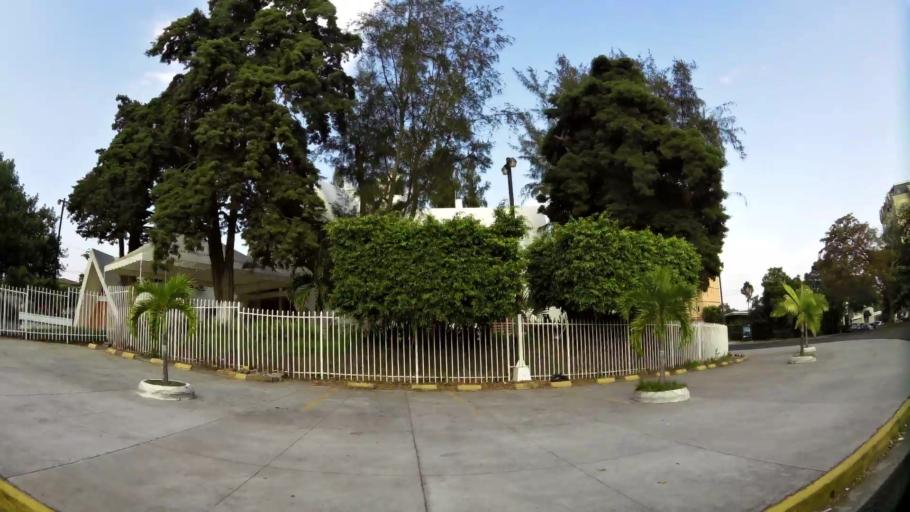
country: SV
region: La Libertad
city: Antiguo Cuscatlan
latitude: 13.6936
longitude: -89.2396
